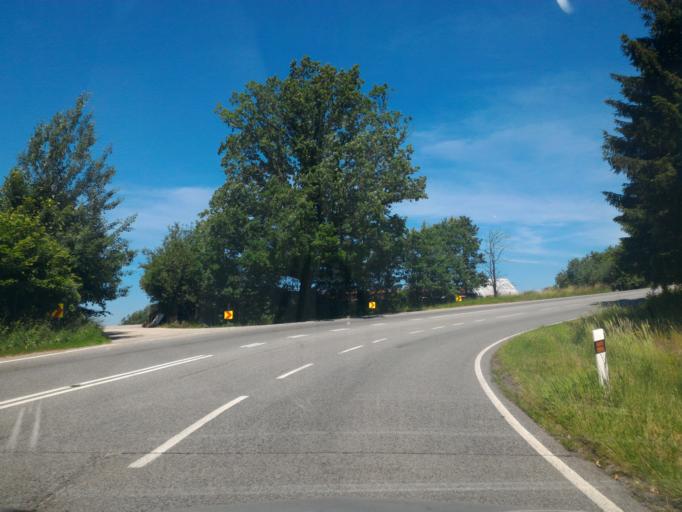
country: CZ
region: Vysocina
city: Dolni Cerekev
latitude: 49.3659
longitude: 15.4939
